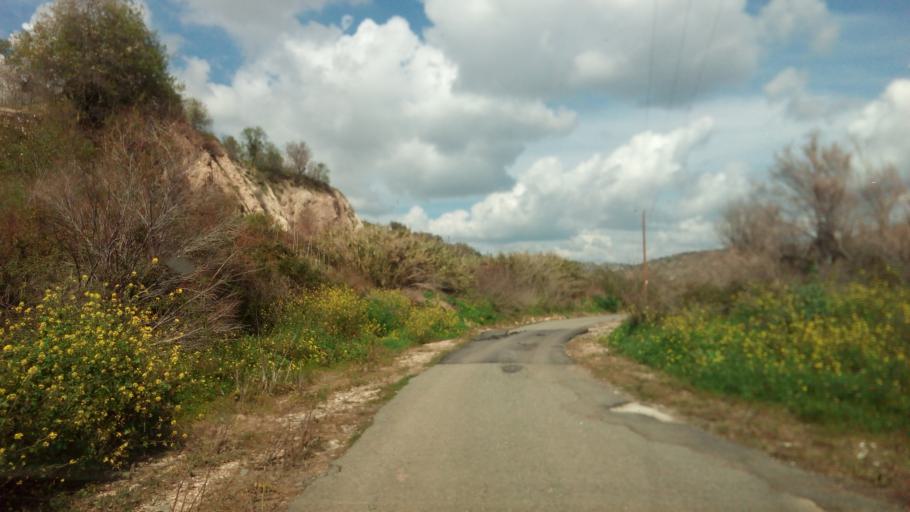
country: CY
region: Pafos
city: Mesogi
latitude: 34.7985
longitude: 32.5288
